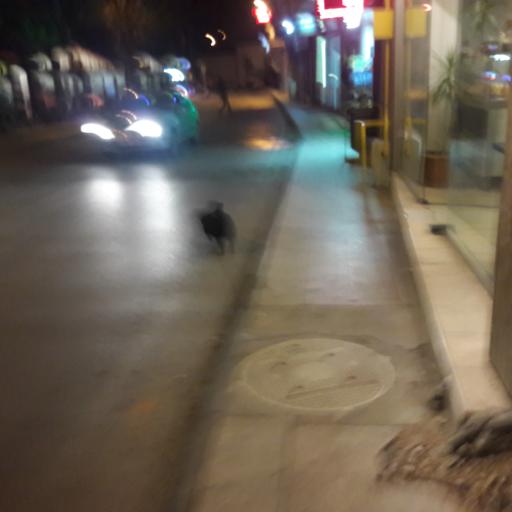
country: TR
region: Sinop
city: Sinop
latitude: 42.0245
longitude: 35.1482
